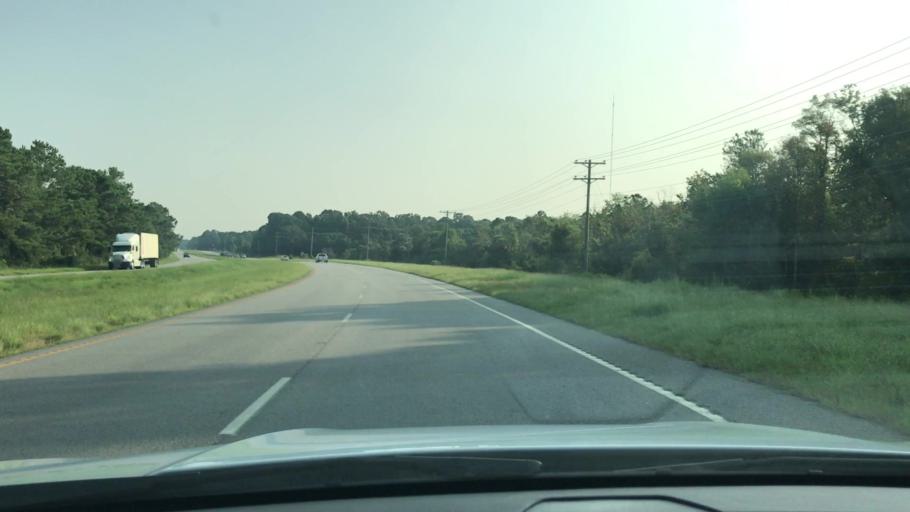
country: US
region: South Carolina
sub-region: Charleston County
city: Isle of Palms
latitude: 32.9185
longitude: -79.7166
